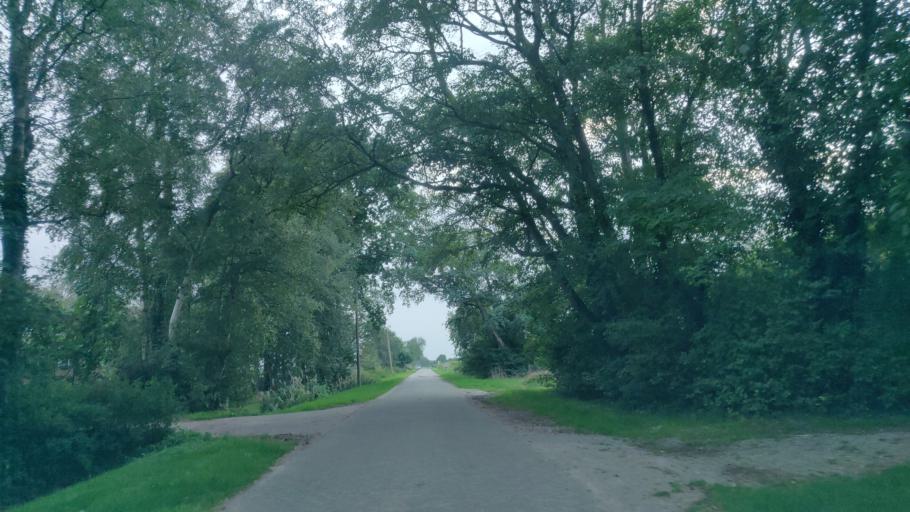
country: DE
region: Lower Saxony
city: Aurich
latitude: 53.5059
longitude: 7.4303
